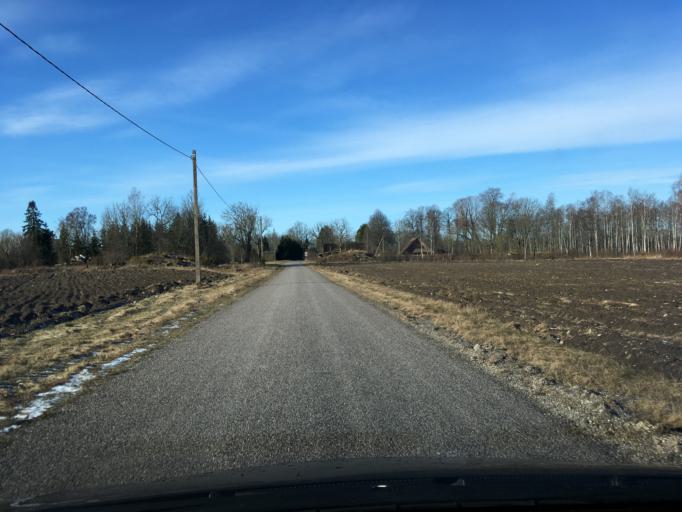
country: EE
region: Laeaene
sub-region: Lihula vald
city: Lihula
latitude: 58.5856
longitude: 23.7106
